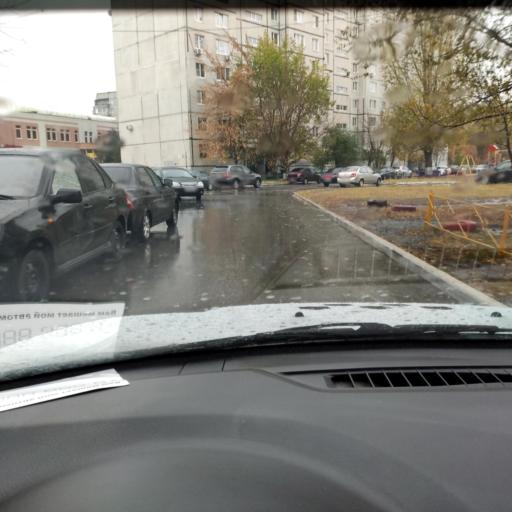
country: RU
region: Samara
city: Tol'yatti
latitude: 53.5409
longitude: 49.4017
